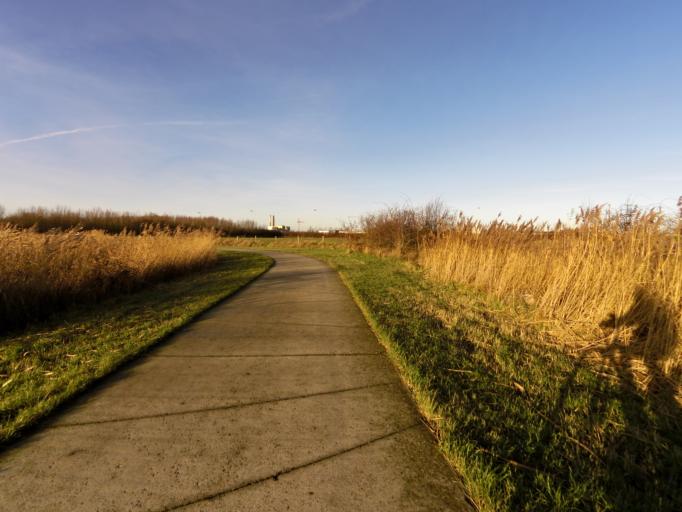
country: BE
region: Flanders
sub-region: Provincie West-Vlaanderen
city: Bredene
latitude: 51.2038
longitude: 2.9708
